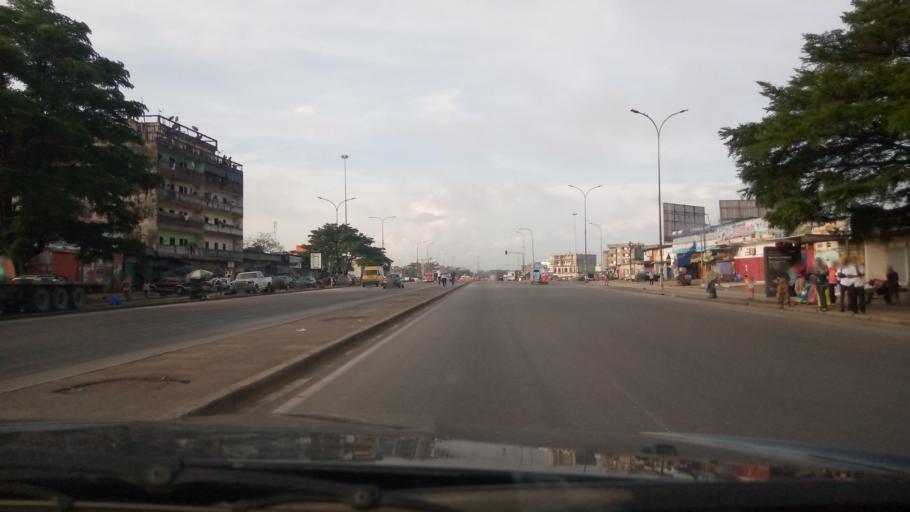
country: CI
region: Lagunes
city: Abobo
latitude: 5.4139
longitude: -4.0161
